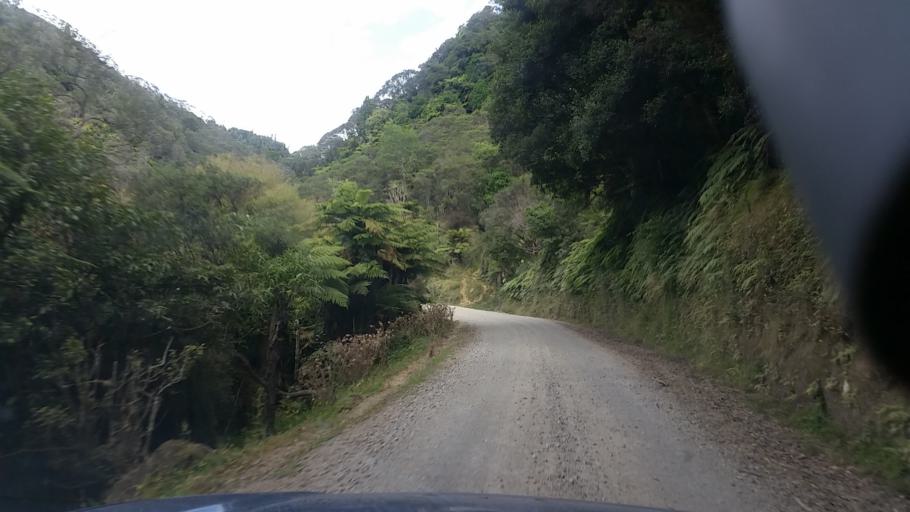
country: NZ
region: Taranaki
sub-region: New Plymouth District
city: Waitara
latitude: -39.0199
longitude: 174.8348
